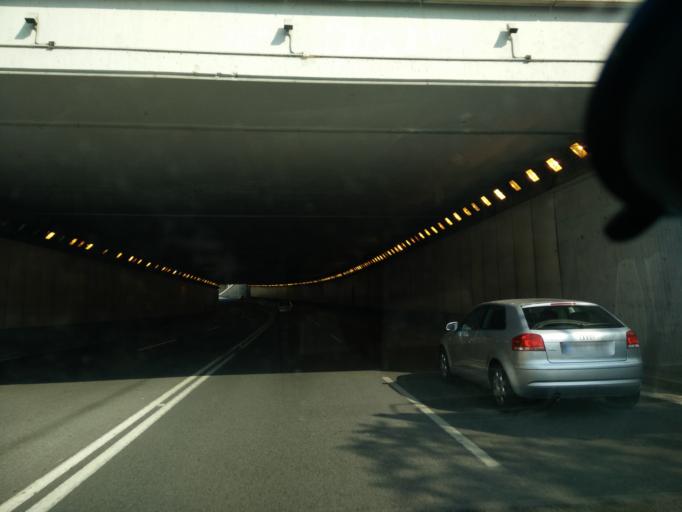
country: ES
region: Catalonia
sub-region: Provincia de Barcelona
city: les Corts
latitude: 41.4005
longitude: 2.1232
